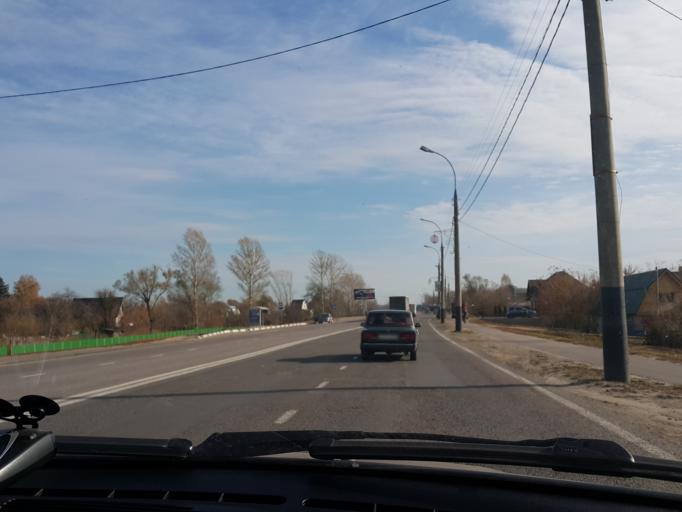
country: RU
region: Tambov
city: Tambov
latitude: 52.7234
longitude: 41.4748
